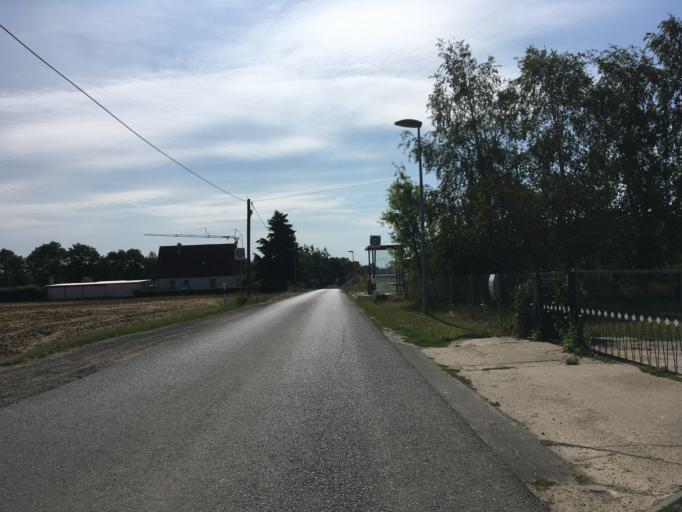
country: DE
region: Brandenburg
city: Gramzow
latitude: 53.2799
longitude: 14.0642
